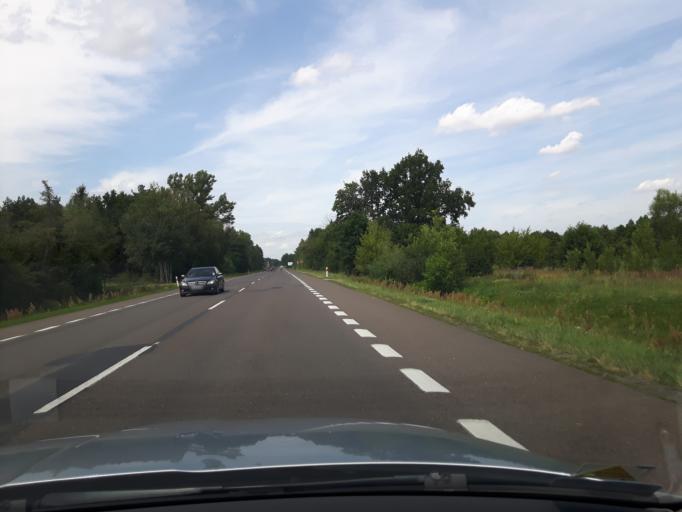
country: PL
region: Masovian Voivodeship
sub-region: Powiat ciechanowski
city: Glinojeck
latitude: 52.8131
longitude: 20.2674
